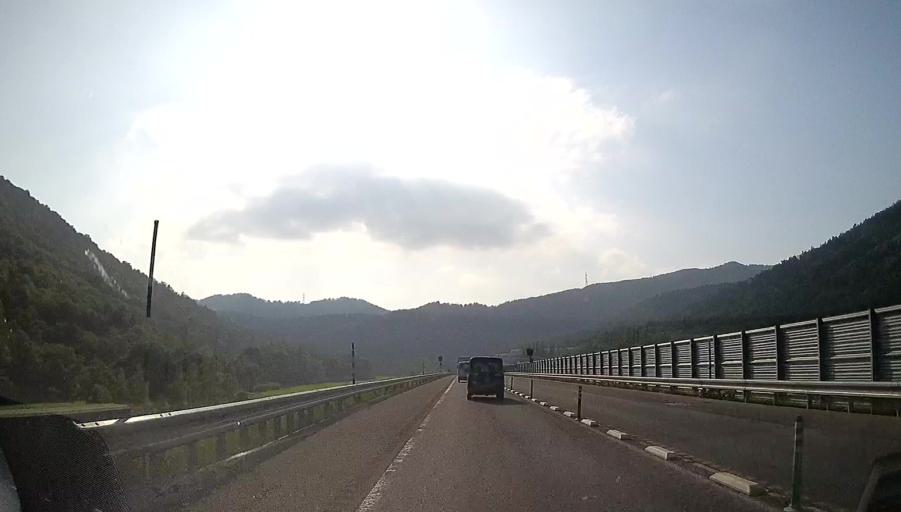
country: JP
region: Hokkaido
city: Shimo-furano
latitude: 43.0637
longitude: 142.5455
